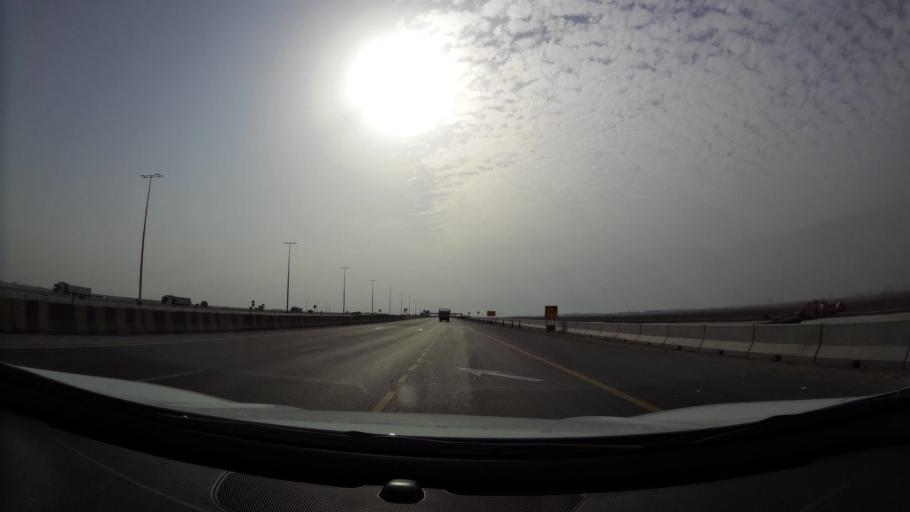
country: AE
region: Abu Dhabi
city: Abu Dhabi
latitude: 24.2825
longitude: 54.5356
